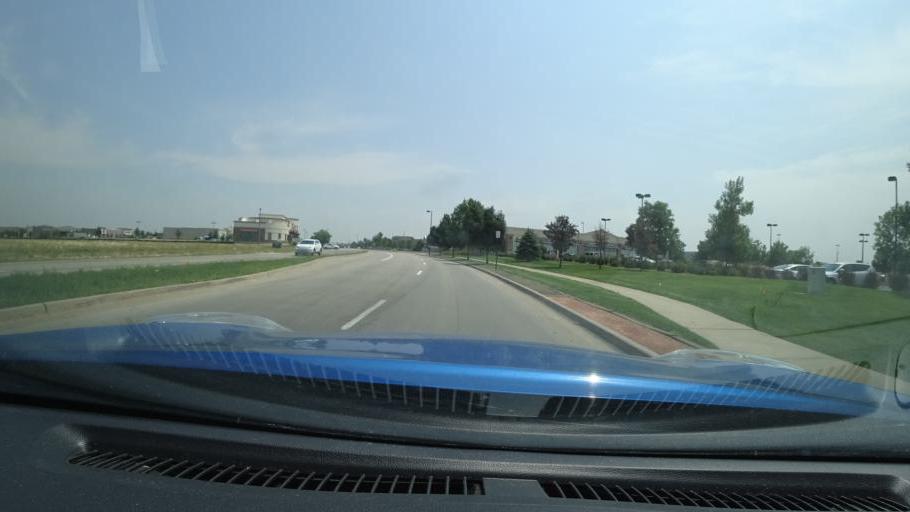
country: US
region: Colorado
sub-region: Adams County
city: Aurora
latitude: 39.7646
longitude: -104.7774
